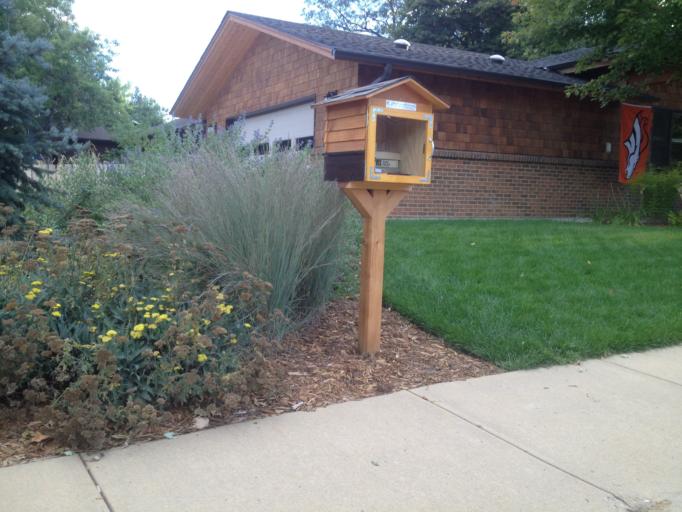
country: US
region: Colorado
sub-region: Boulder County
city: Louisville
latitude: 39.9709
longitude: -105.1347
